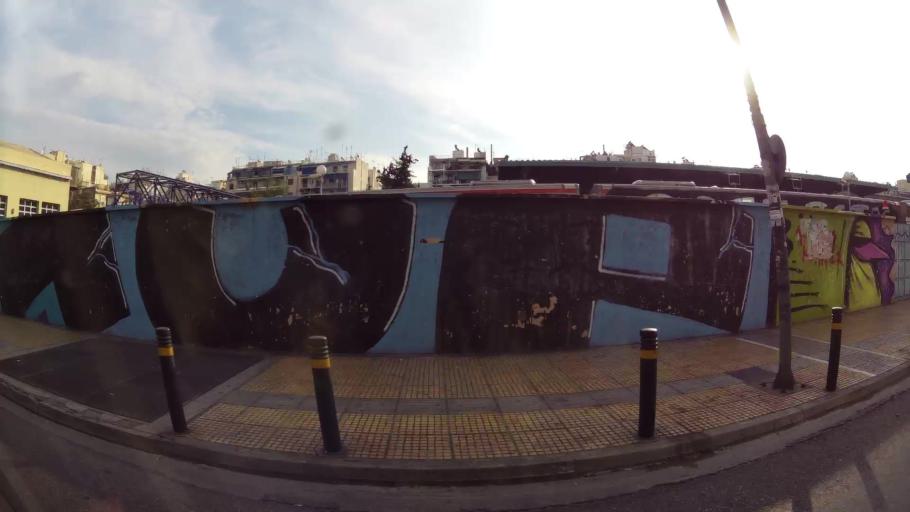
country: GR
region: Attica
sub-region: Nomarchia Athinas
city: Kipseli
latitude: 37.9995
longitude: 23.7224
